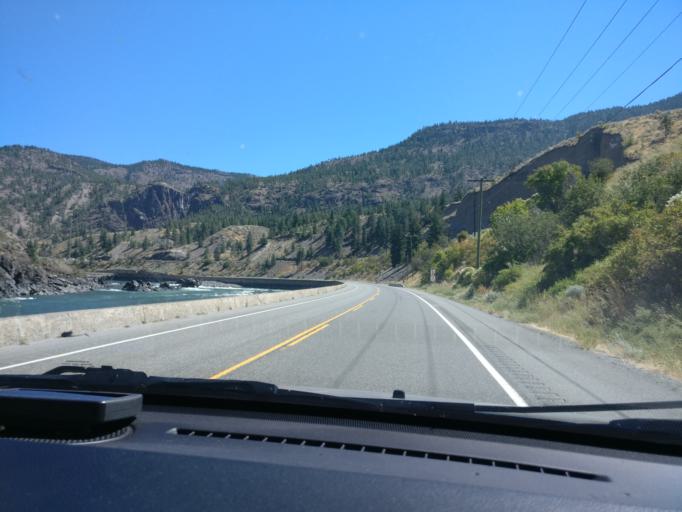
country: CA
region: British Columbia
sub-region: Thompson-Nicola Regional District
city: Ashcroft
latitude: 50.2631
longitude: -121.4114
